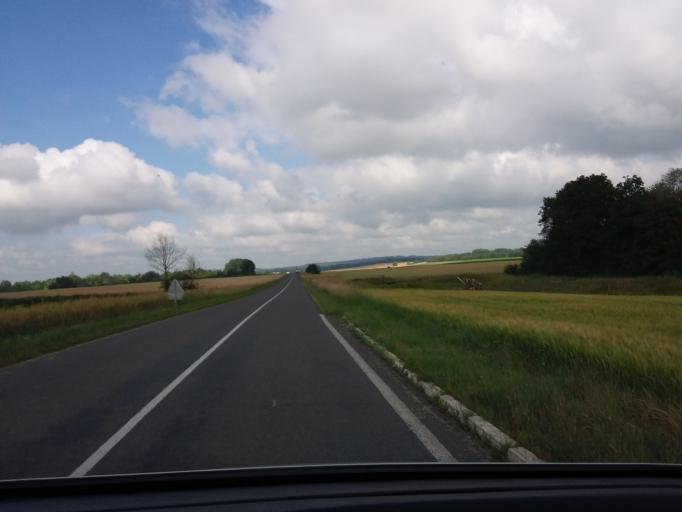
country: FR
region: Champagne-Ardenne
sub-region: Departement de la Marne
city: Cormicy
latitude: 49.4098
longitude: 3.8527
